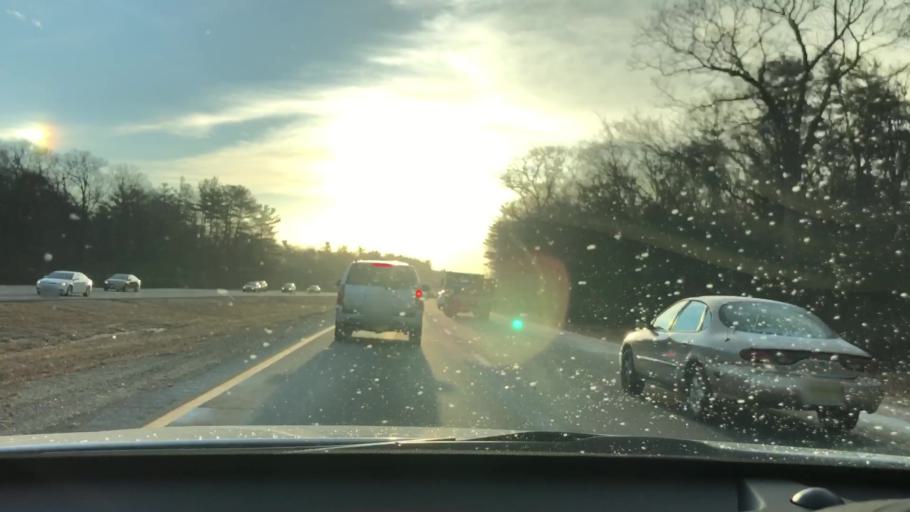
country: US
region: Massachusetts
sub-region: Norfolk County
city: Weymouth
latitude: 42.1821
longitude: -70.9193
